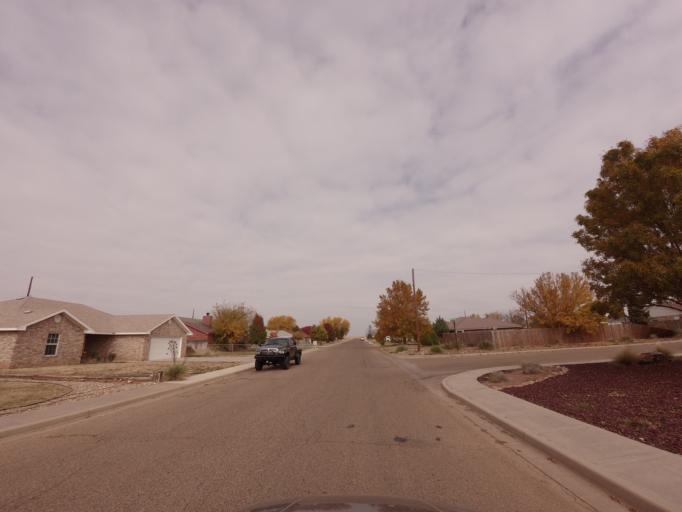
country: US
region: New Mexico
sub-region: Curry County
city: Clovis
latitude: 34.4313
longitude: -103.2268
